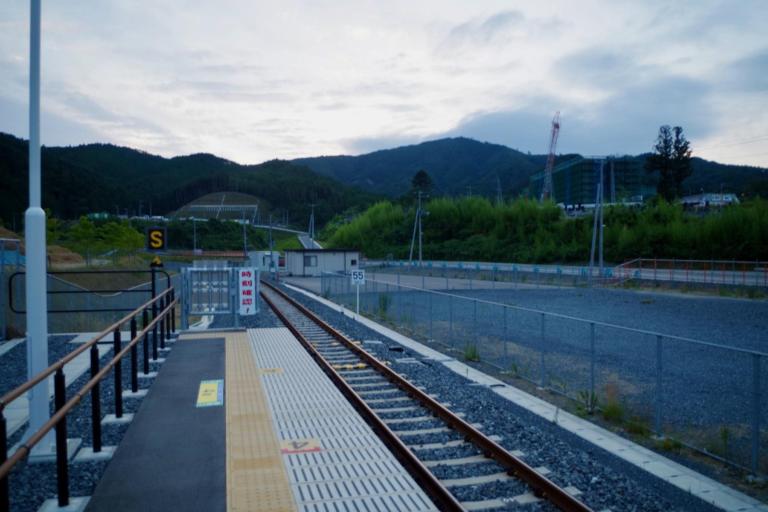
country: JP
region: Miyagi
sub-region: Oshika Gun
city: Onagawa Cho
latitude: 38.4469
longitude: 141.4427
